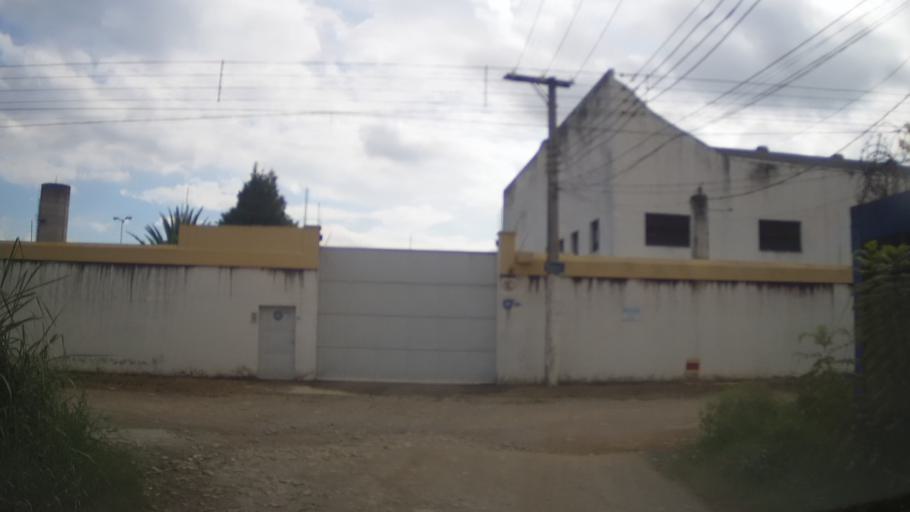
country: BR
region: Sao Paulo
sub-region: Guarulhos
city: Guarulhos
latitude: -23.4625
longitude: -46.4868
